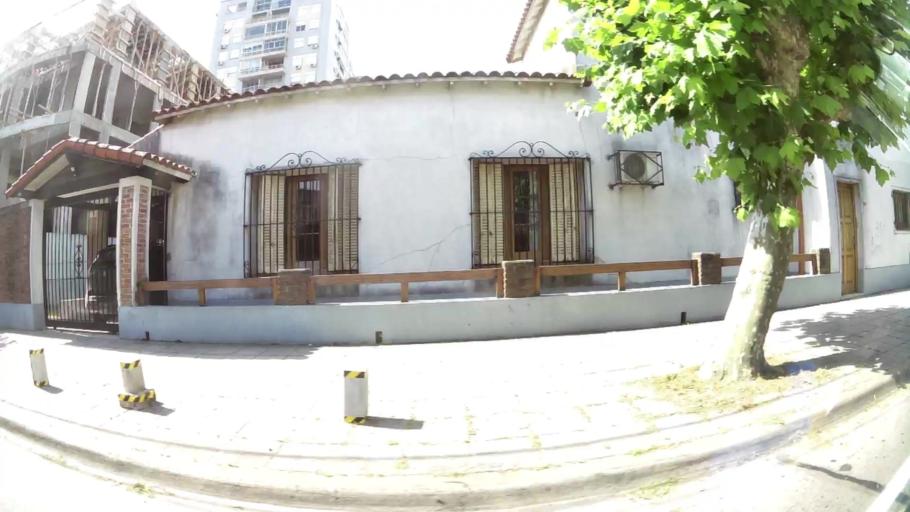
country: AR
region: Buenos Aires
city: San Justo
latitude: -34.6410
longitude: -58.5563
